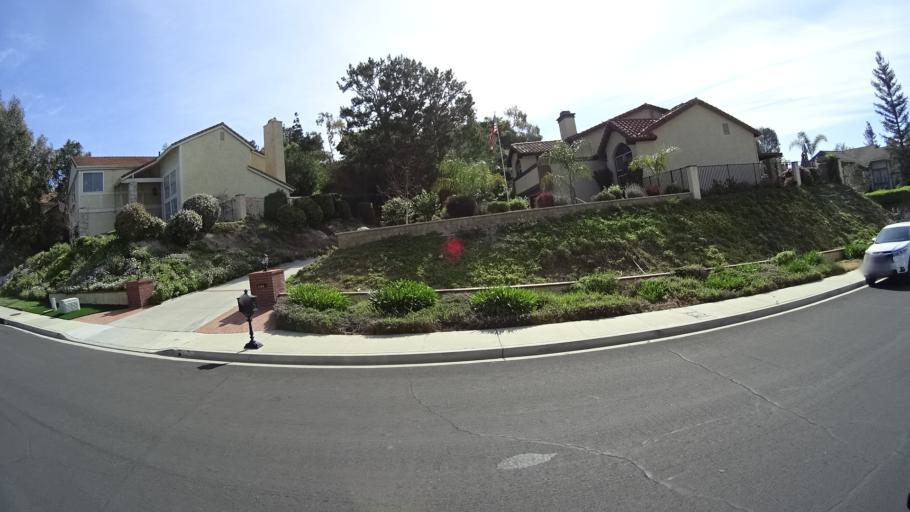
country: US
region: California
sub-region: Ventura County
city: Thousand Oaks
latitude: 34.2216
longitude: -118.8412
